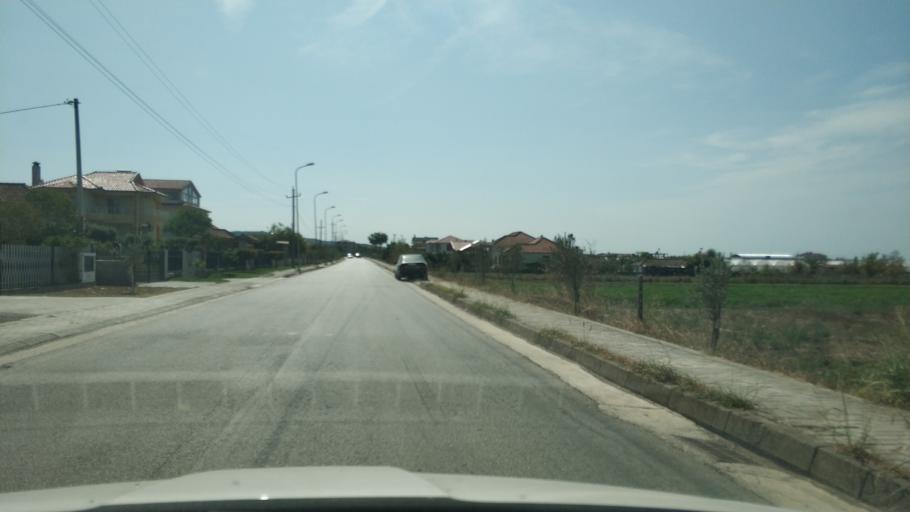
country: AL
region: Fier
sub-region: Rrethi i Lushnjes
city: Divjake
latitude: 40.9816
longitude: 19.5348
